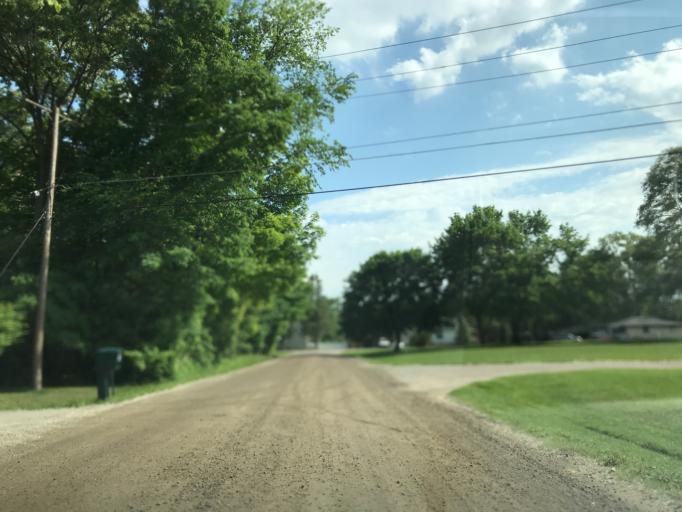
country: US
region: Michigan
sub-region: Oakland County
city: Farmington
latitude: 42.4542
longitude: -83.3296
